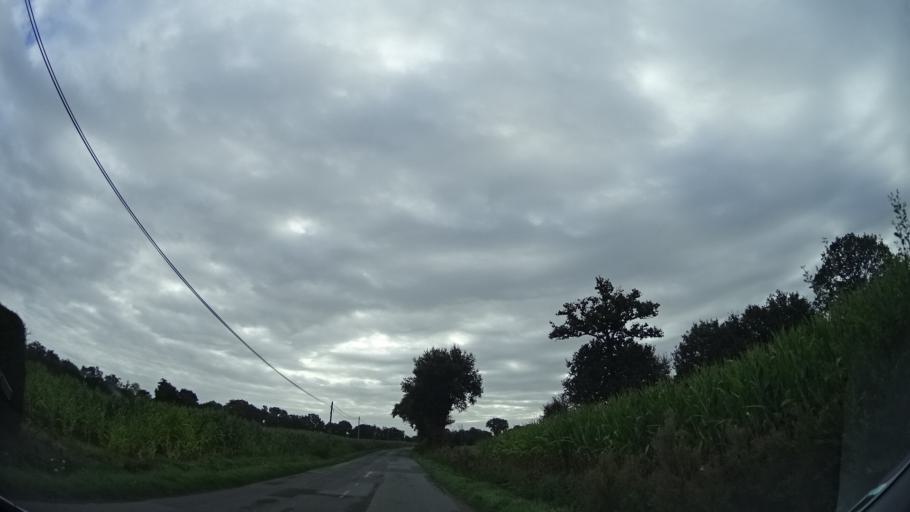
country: FR
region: Brittany
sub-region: Departement d'Ille-et-Vilaine
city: Dinge
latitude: 48.3557
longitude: -1.7017
